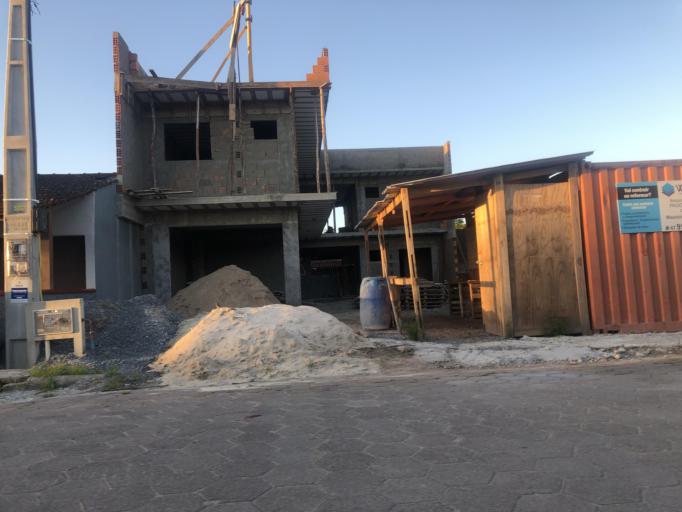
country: BR
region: Santa Catarina
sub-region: Sao Francisco Do Sul
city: Sao Francisco do Sul
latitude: -26.2168
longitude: -48.5275
